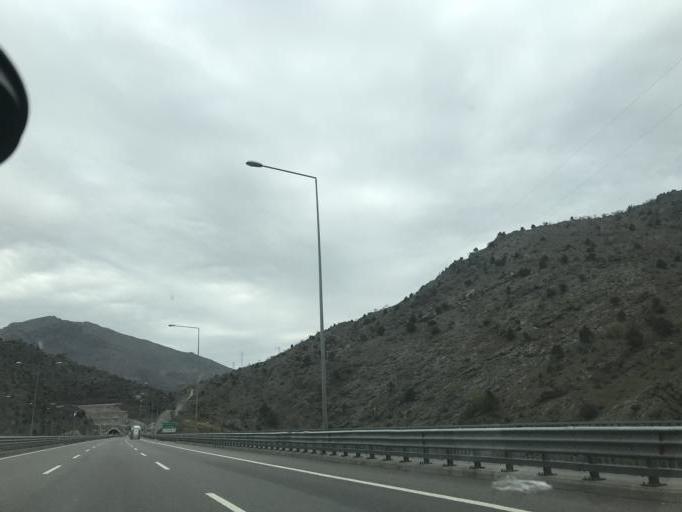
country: TR
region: Nigde
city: Ciftehan
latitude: 37.5534
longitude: 34.7742
